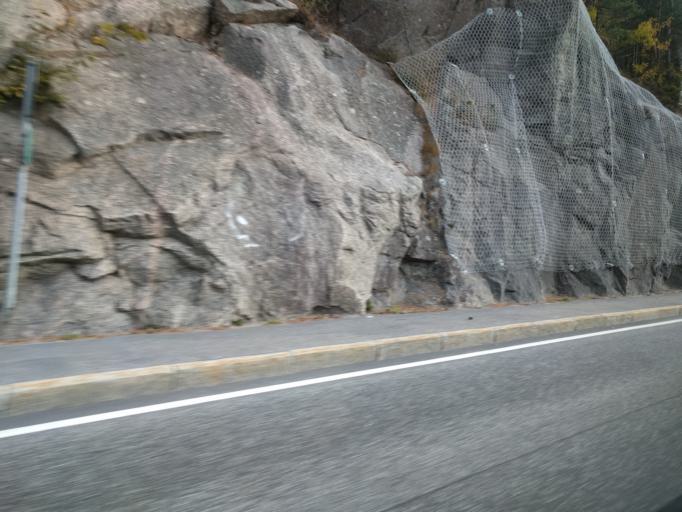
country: NO
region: Vest-Agder
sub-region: Songdalen
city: Nodeland
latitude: 58.2967
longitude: 7.8343
